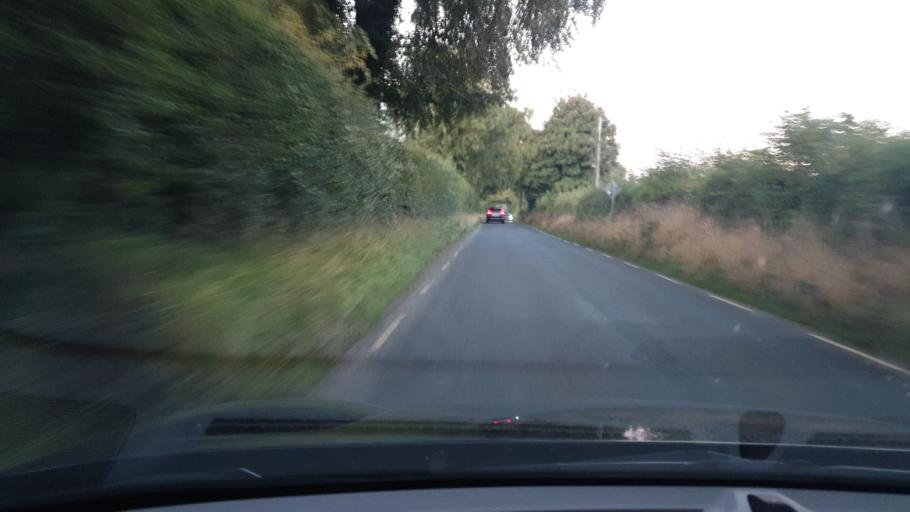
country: IE
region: Leinster
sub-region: Kildare
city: Clane
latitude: 53.3413
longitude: -6.7160
